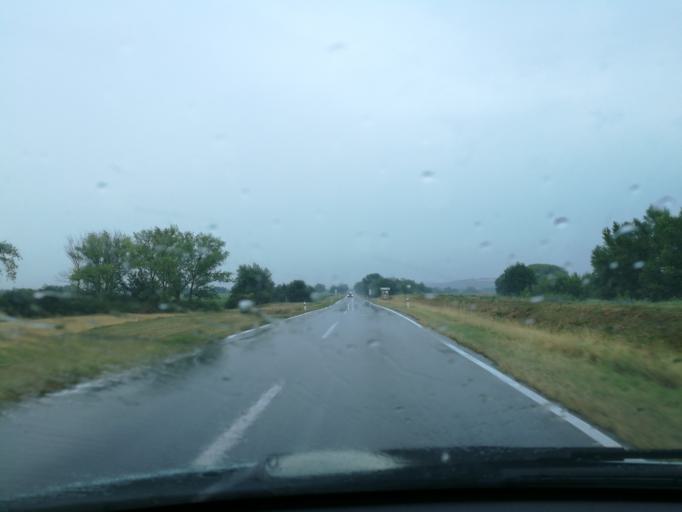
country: HU
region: Komarom-Esztergom
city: Almasfuzito
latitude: 47.7435
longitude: 18.2566
